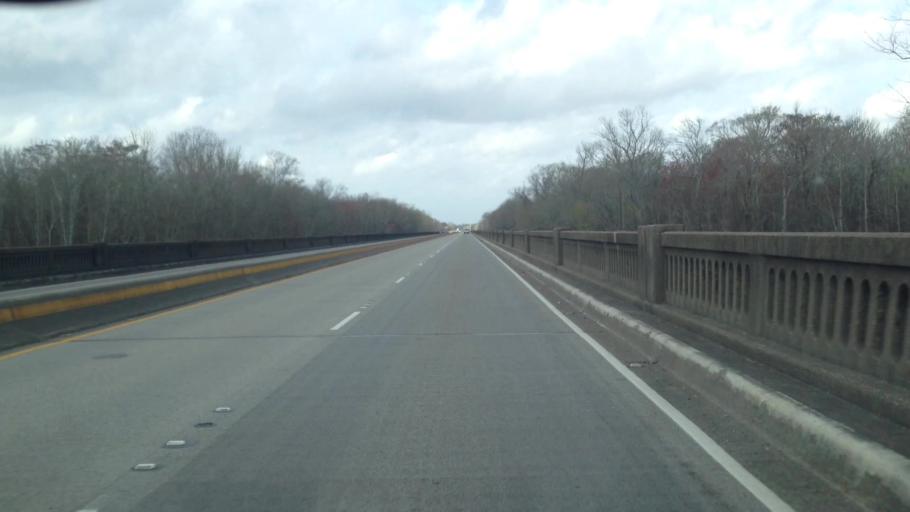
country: US
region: Louisiana
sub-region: Saint Landry Parish
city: Krotz Springs
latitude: 30.5533
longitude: -91.7079
